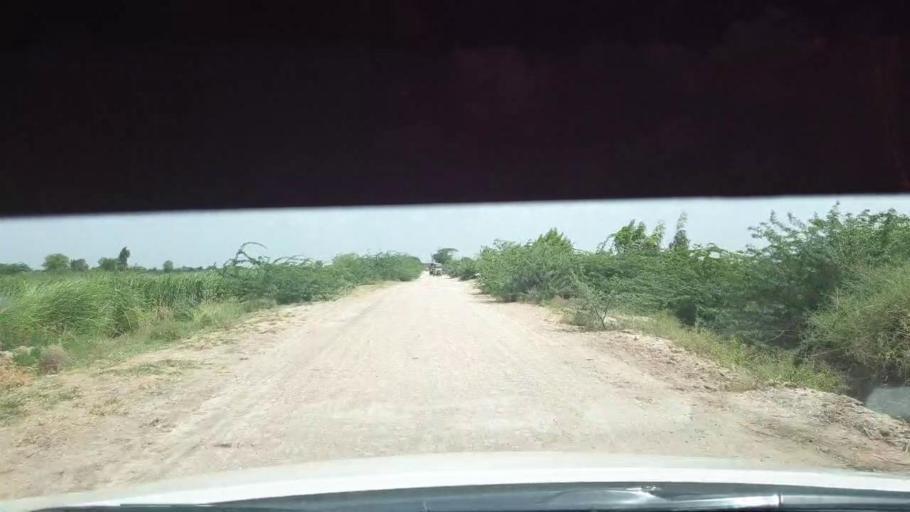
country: PK
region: Sindh
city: Kadhan
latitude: 24.4963
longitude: 68.9824
